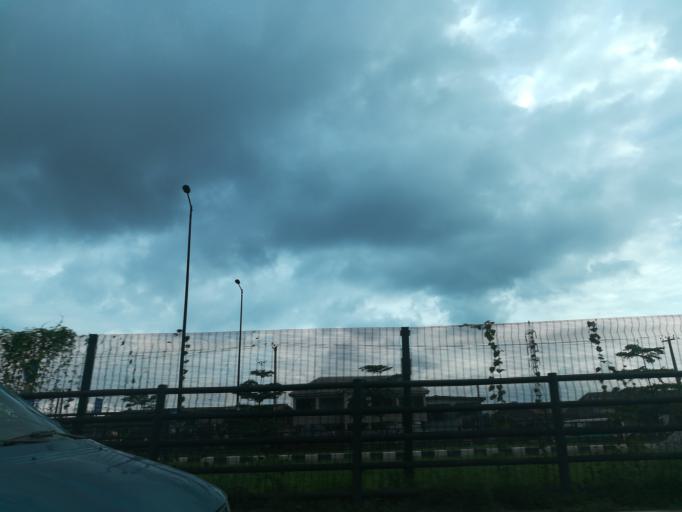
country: NG
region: Lagos
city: Ebute Ikorodu
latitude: 6.6097
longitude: 3.4318
